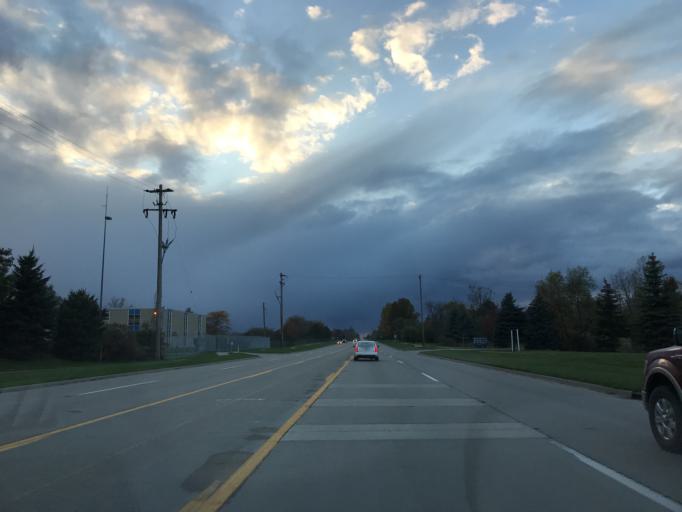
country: US
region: Michigan
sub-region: Oakland County
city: Farmington
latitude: 42.4398
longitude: -83.4049
